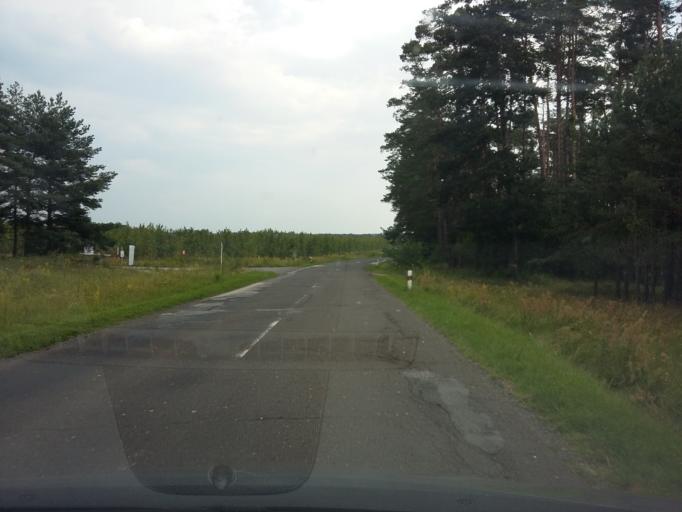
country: SK
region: Bratislavsky
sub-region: Okres Malacky
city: Malacky
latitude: 48.4543
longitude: 17.1097
